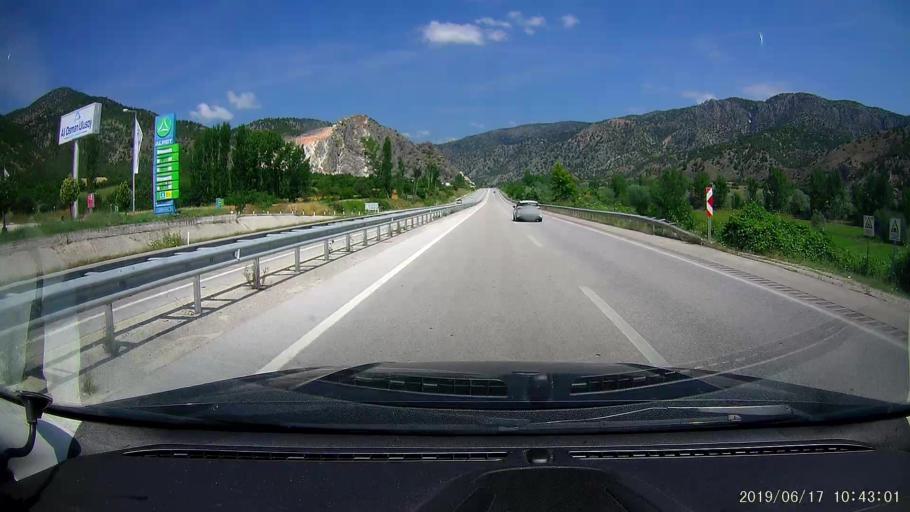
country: TR
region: Corum
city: Kargi
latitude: 41.0568
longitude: 34.5430
